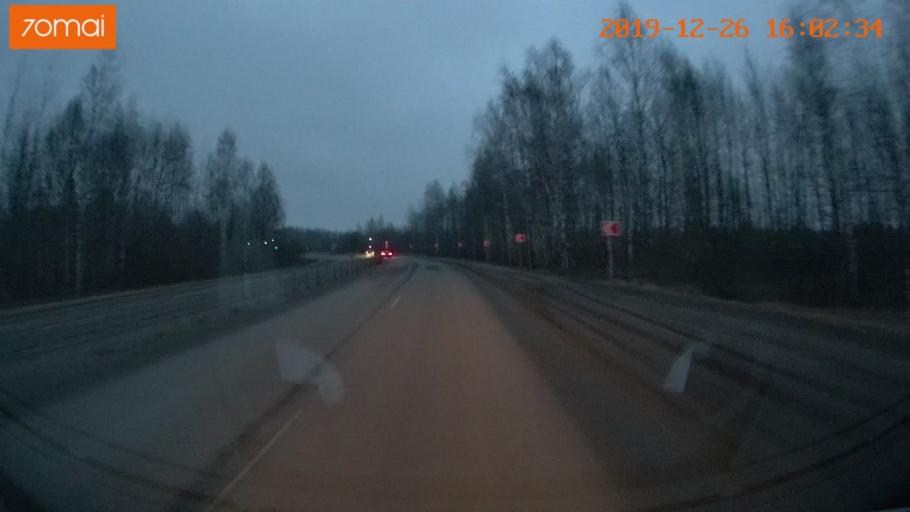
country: RU
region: Jaroslavl
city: Rybinsk
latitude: 58.0108
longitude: 38.8374
